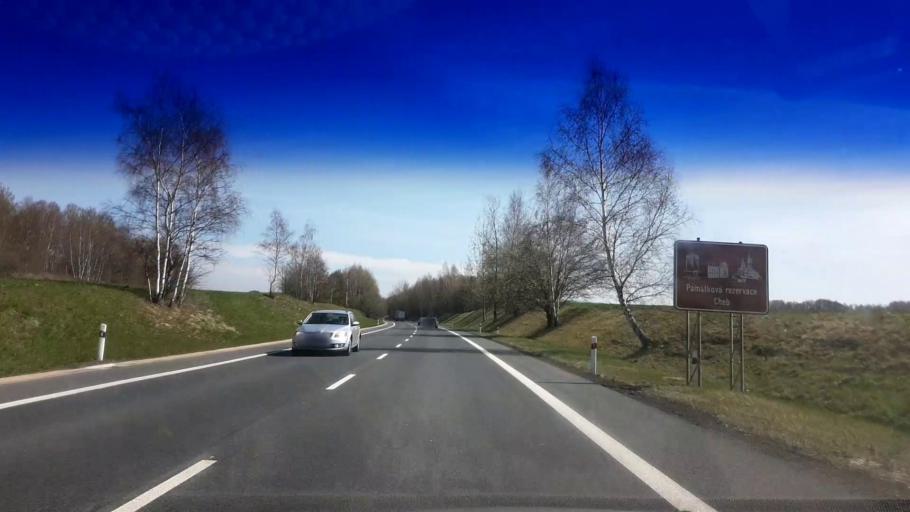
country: CZ
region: Karlovarsky
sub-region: Okres Cheb
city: Frantiskovy Lazne
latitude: 50.0948
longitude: 12.3437
